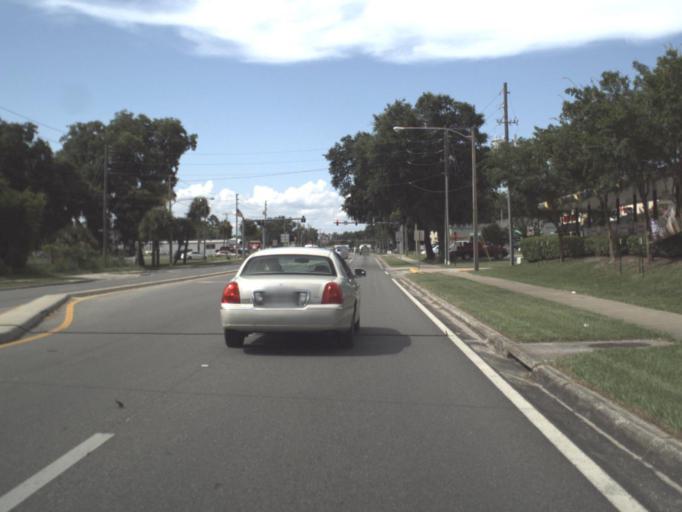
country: US
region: Florida
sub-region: Taylor County
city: Perry
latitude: 30.1015
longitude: -83.5829
